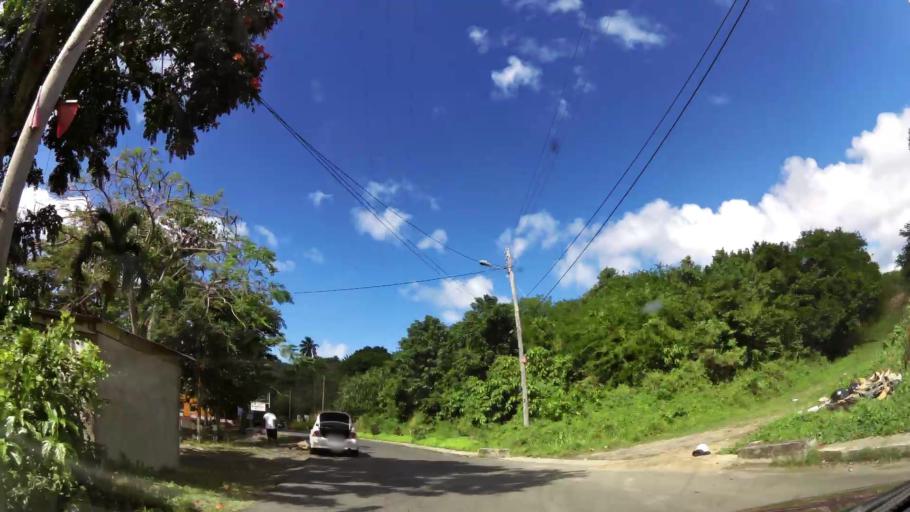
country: DM
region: Saint John
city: Portsmouth
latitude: 15.5837
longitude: -61.4613
